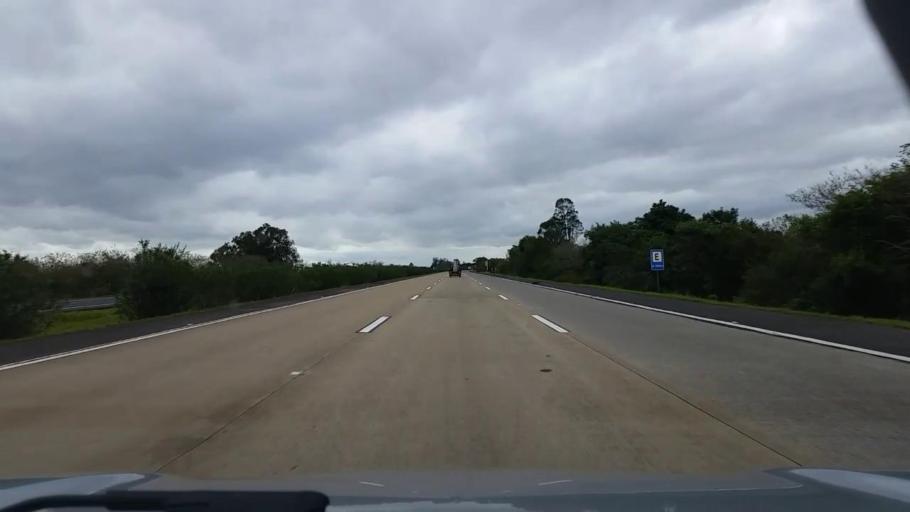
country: BR
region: Rio Grande do Sul
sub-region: Rolante
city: Rolante
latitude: -29.8855
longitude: -50.5830
